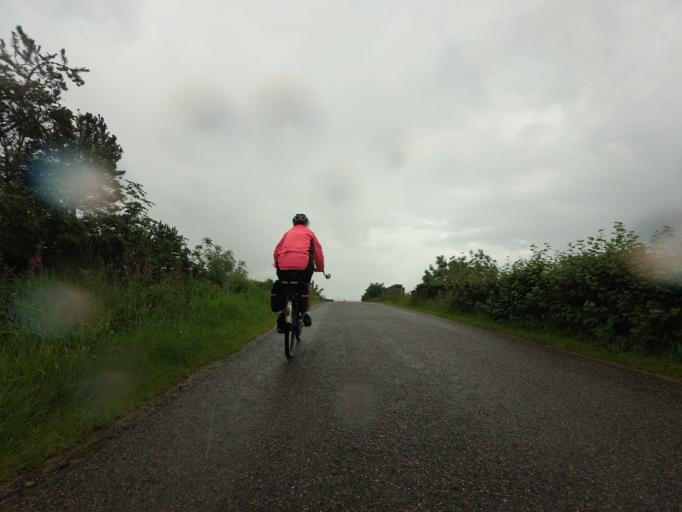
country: GB
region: Scotland
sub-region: Moray
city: Fochabers
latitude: 57.6629
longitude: -3.0731
